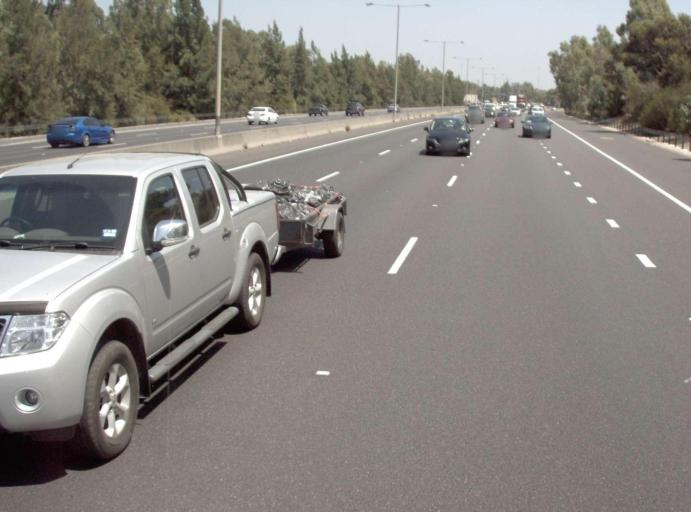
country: AU
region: Victoria
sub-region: Boroondara
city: Balwyn North
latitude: -37.7798
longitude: 145.0885
